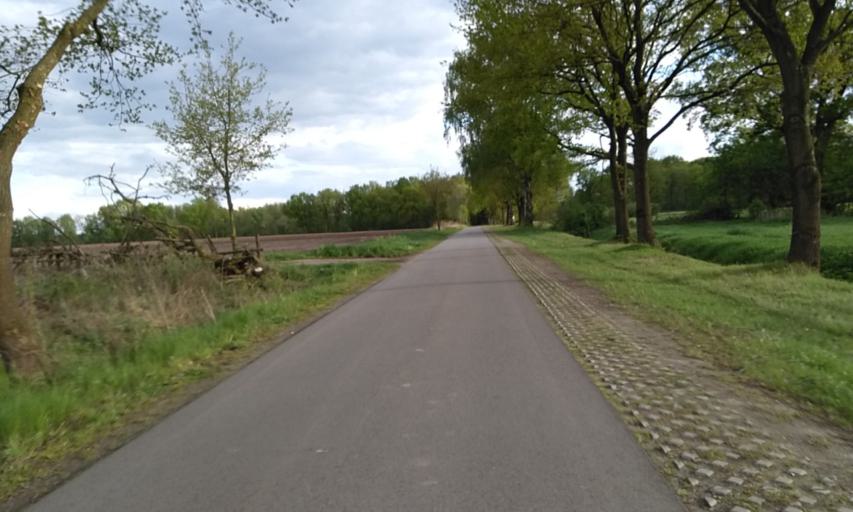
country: DE
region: Lower Saxony
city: Sauensiek
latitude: 53.3951
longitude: 9.5630
